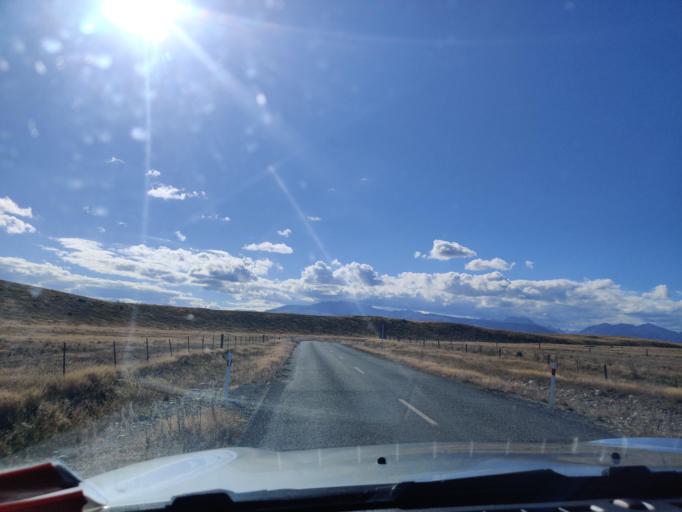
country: NZ
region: Canterbury
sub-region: Timaru District
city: Pleasant Point
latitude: -43.9932
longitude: 170.4513
